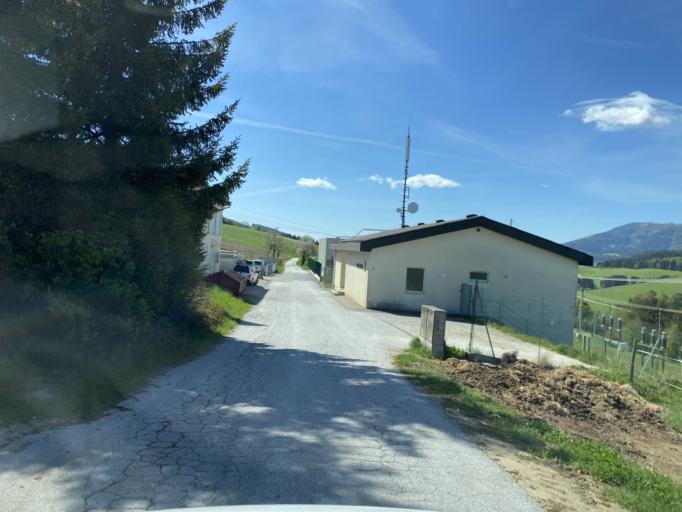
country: AT
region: Styria
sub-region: Politischer Bezirk Weiz
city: Birkfeld
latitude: 47.3455
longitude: 15.6909
